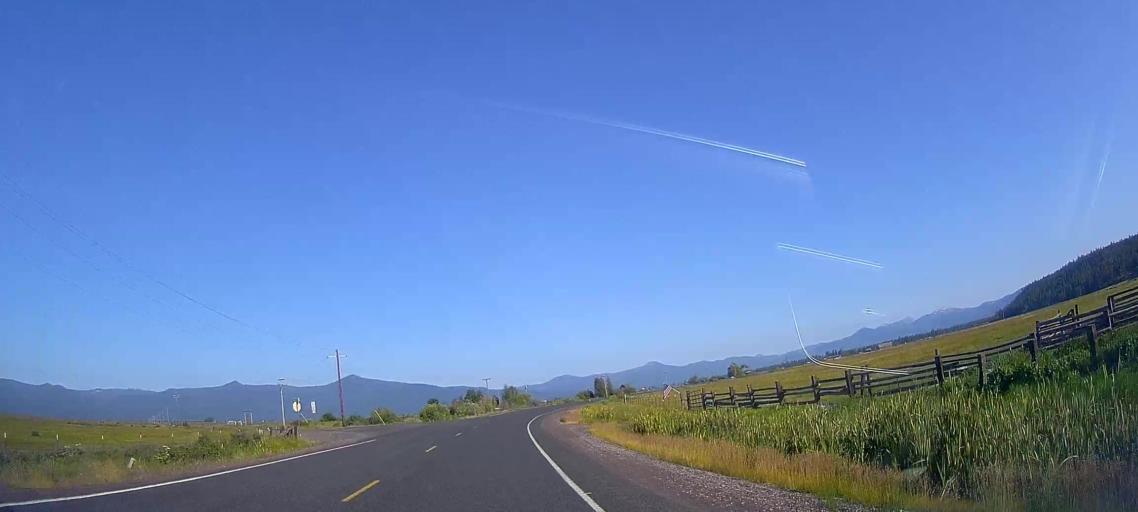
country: US
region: Oregon
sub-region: Klamath County
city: Klamath Falls
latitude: 42.6464
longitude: -121.9517
